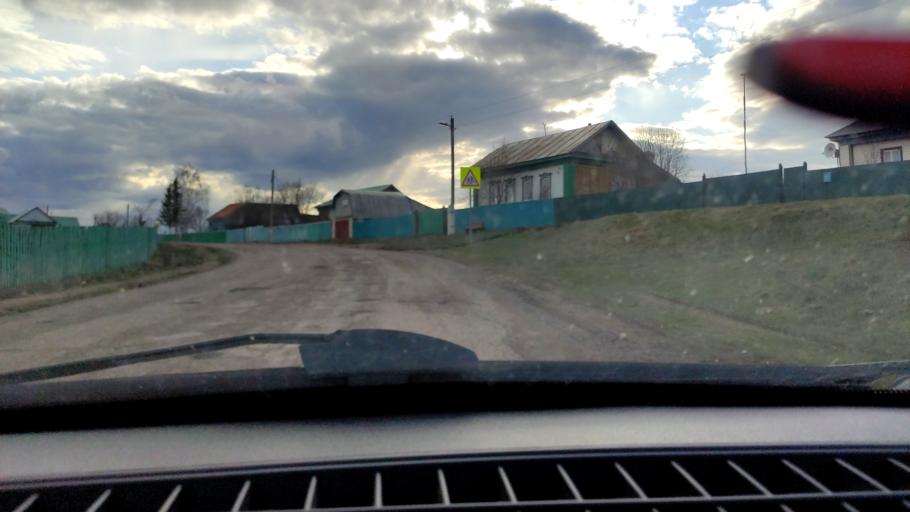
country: RU
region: Bashkortostan
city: Karmaskaly
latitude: 54.3360
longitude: 56.0047
